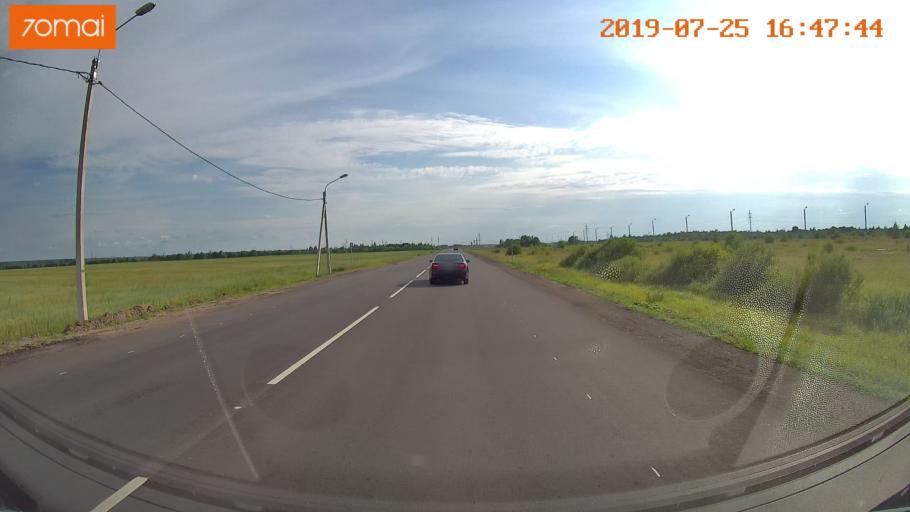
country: RU
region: Ivanovo
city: Privolzhsk
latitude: 57.3639
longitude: 41.2691
